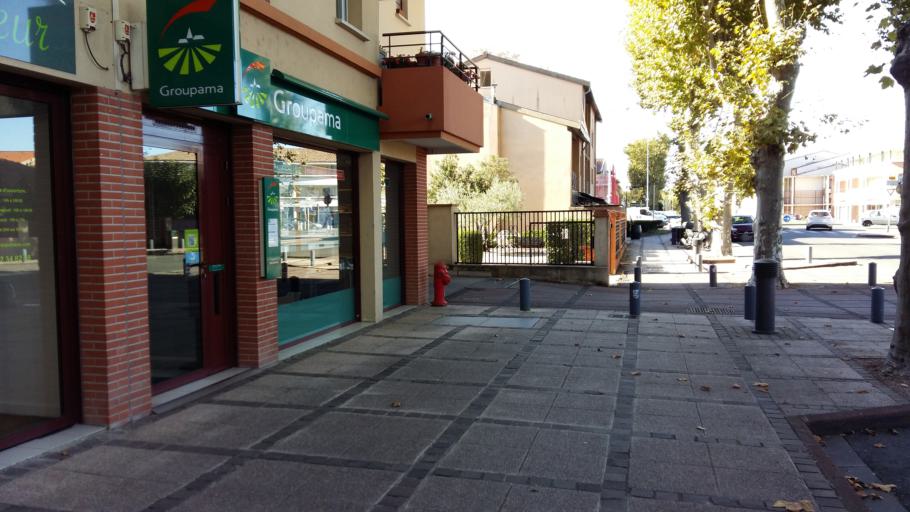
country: FR
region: Midi-Pyrenees
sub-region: Departement de la Haute-Garonne
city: Tournefeuille
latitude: 43.5840
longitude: 1.3445
